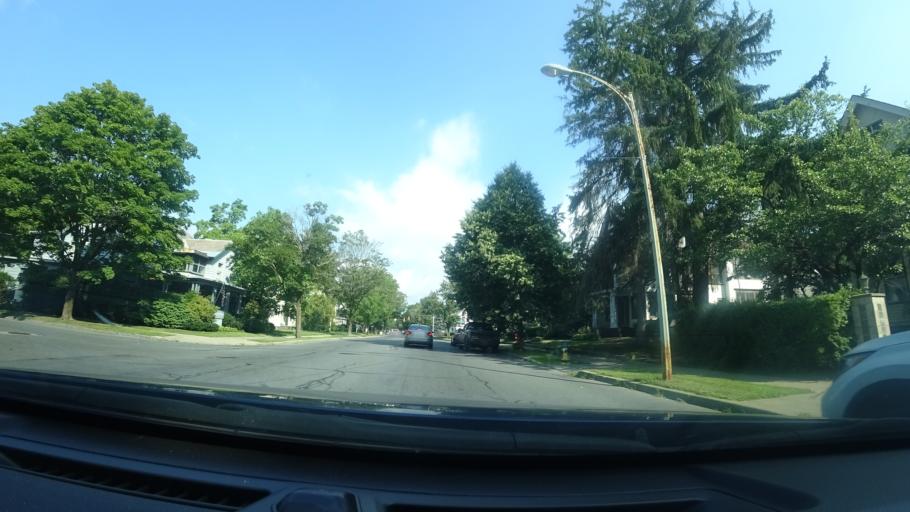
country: US
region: New York
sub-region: Warren County
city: Glens Falls
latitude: 43.3154
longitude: -73.6530
